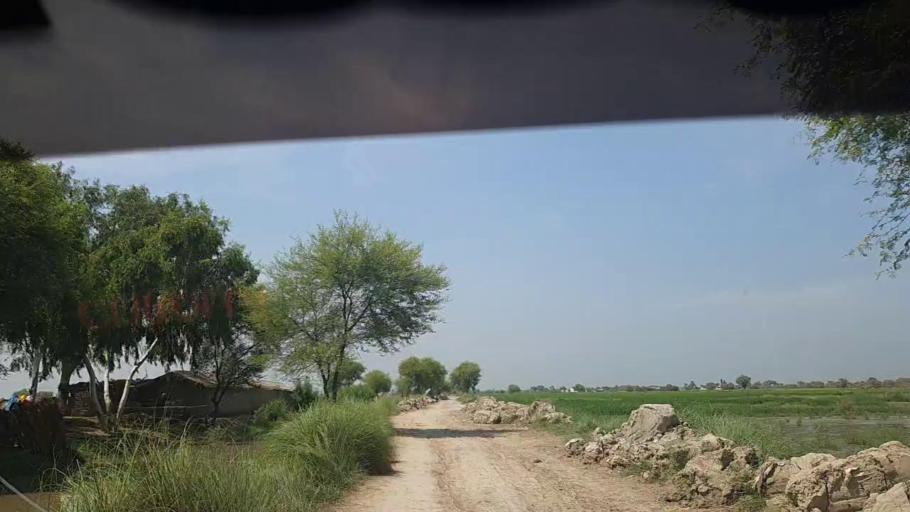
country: PK
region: Sindh
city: Thul
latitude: 28.1843
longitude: 68.7218
